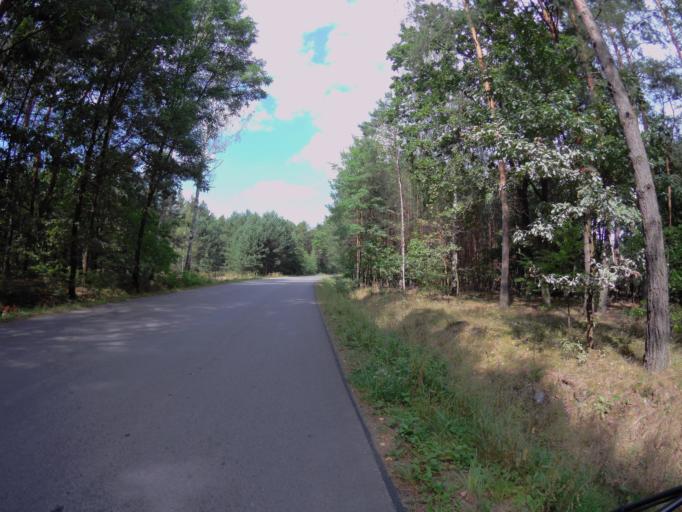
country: PL
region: Subcarpathian Voivodeship
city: Nowa Sarzyna
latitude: 50.2763
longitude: 22.3526
